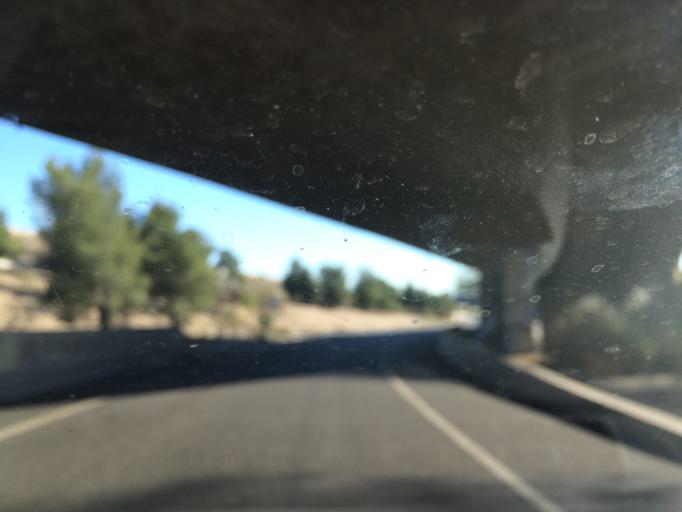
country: ES
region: Madrid
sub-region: Provincia de Madrid
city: Las Tablas
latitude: 40.5086
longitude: -3.6594
